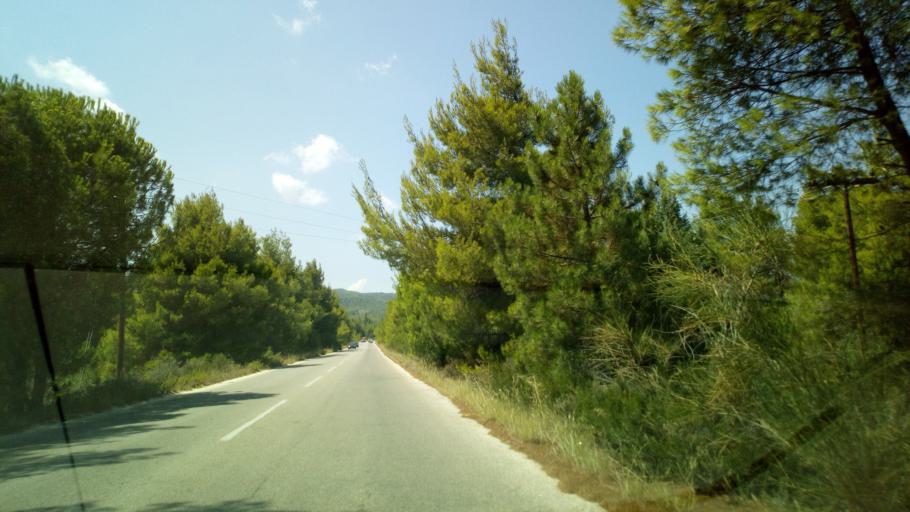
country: GR
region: Central Macedonia
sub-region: Nomos Chalkidikis
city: Sarti
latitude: 40.1296
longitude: 23.9355
